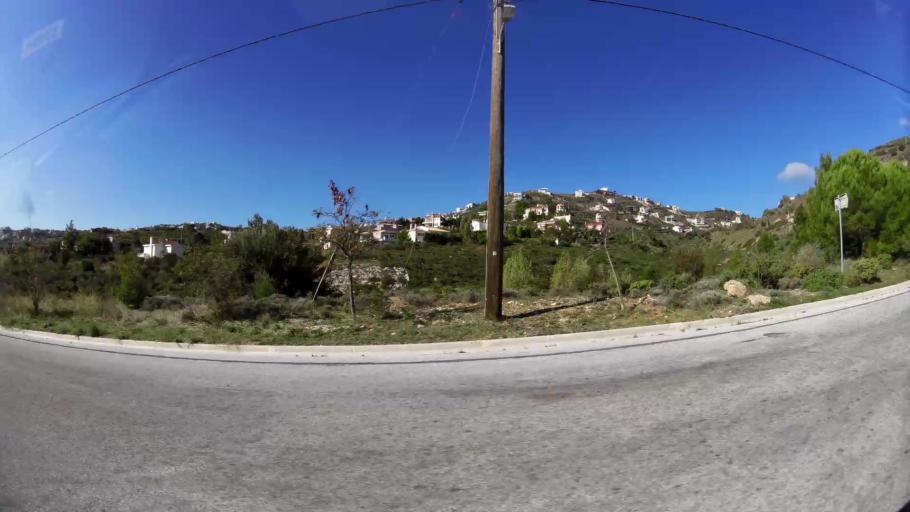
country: GR
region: Attica
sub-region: Nomarchia Anatolikis Attikis
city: Dhrafi
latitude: 38.0389
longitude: 23.9048
